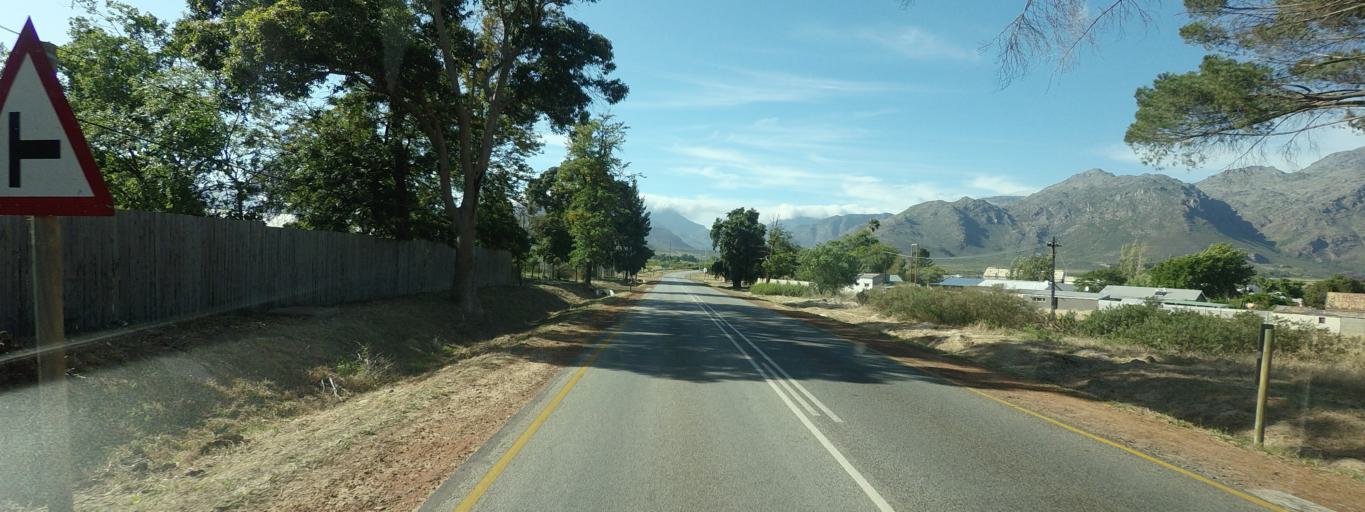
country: ZA
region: Western Cape
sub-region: Cape Winelands District Municipality
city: Paarl
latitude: -33.8705
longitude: 19.0433
